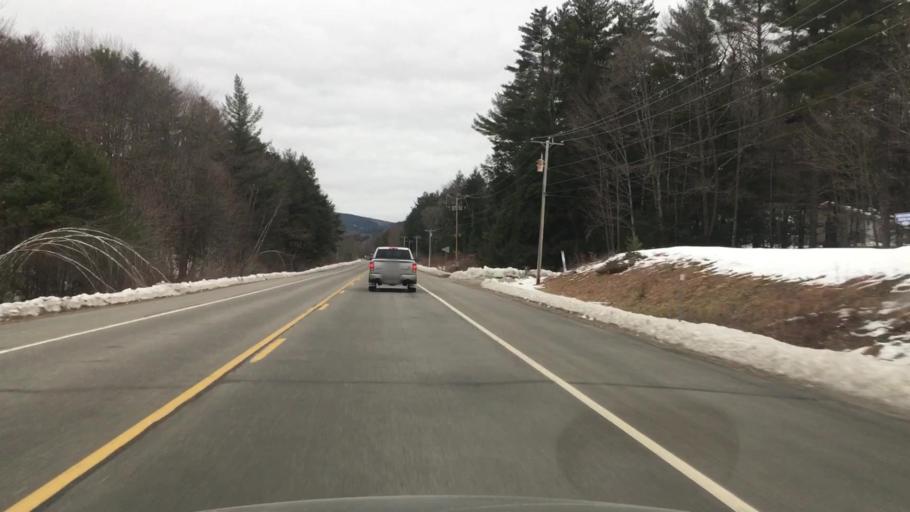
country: US
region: New Hampshire
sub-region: Merrimack County
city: Newbury
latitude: 43.2975
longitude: -71.9975
